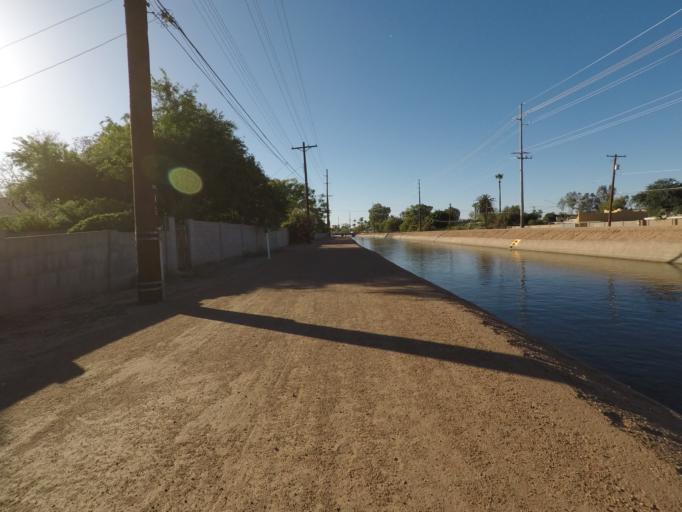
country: US
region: Arizona
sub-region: Maricopa County
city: Paradise Valley
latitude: 33.4978
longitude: -111.9793
